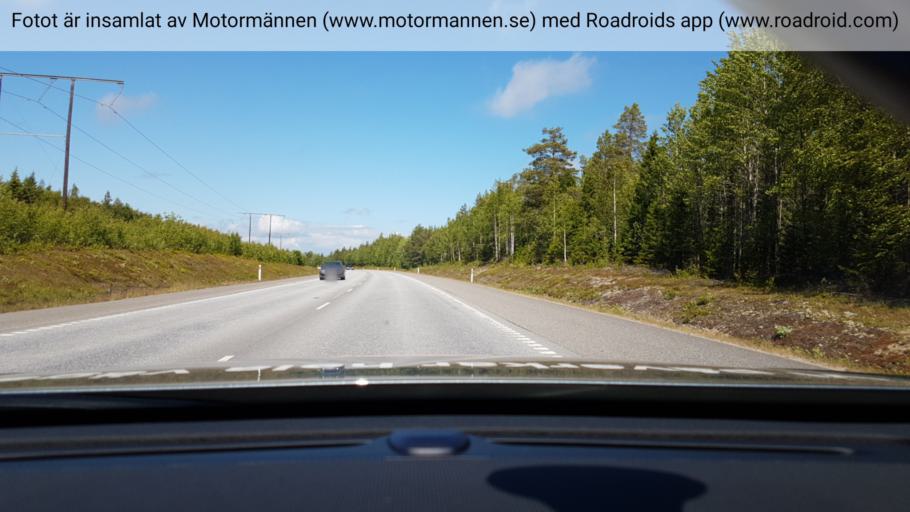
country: SE
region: Vaesterbotten
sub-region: Umea Kommun
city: Holmsund
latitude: 63.7479
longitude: 20.3773
